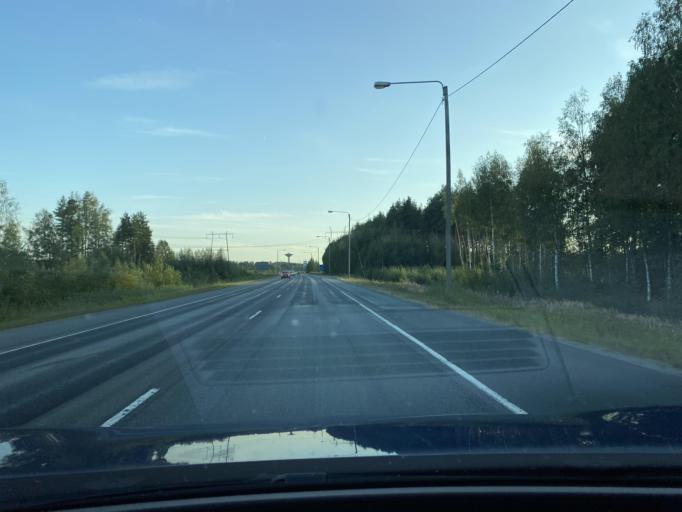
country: FI
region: Southern Ostrobothnia
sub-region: Seinaejoki
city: Nurmo
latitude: 62.8173
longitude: 22.9026
